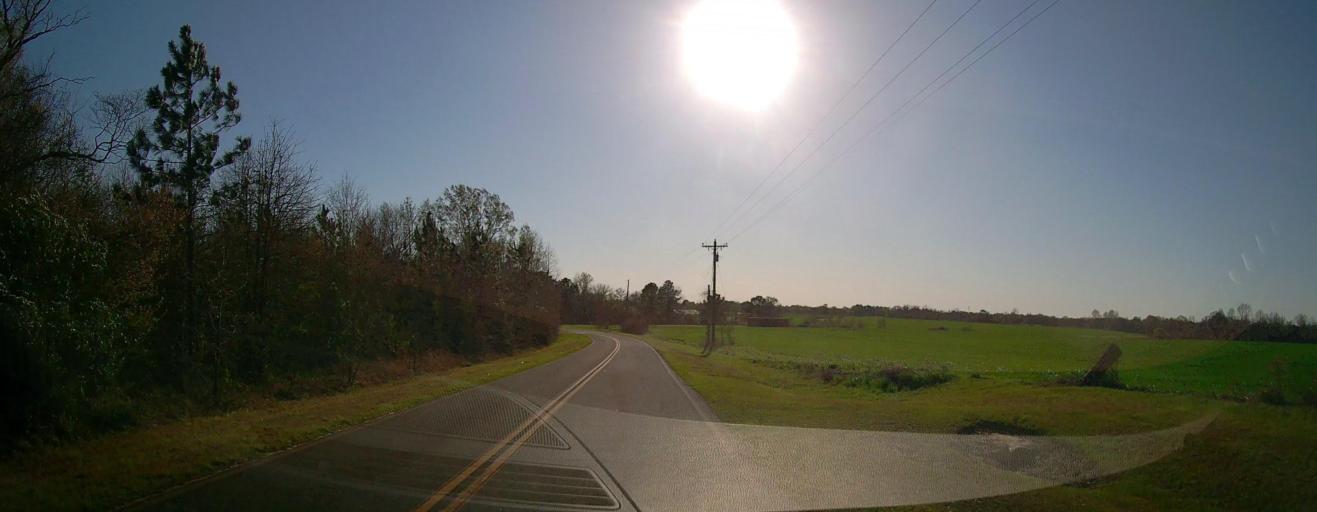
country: US
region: Georgia
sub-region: Pulaski County
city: Hawkinsville
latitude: 32.3239
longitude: -83.5677
